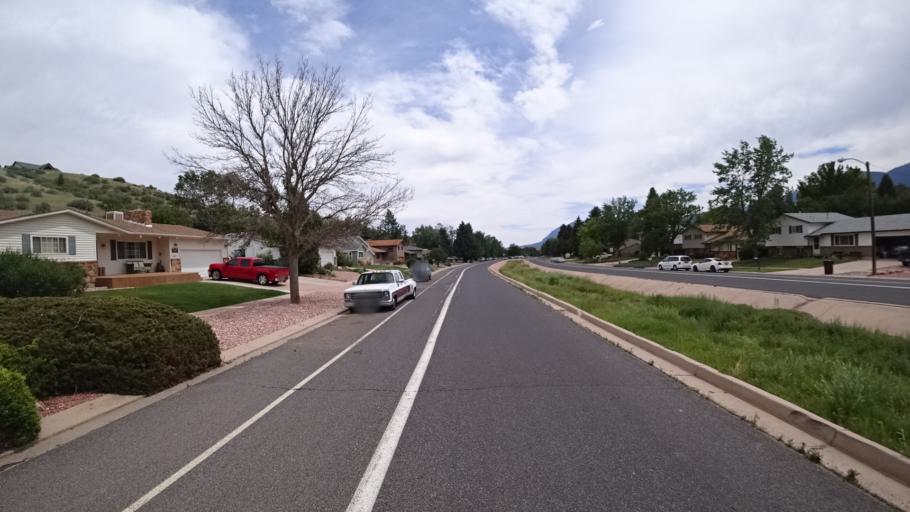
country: US
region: Colorado
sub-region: El Paso County
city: Manitou Springs
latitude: 38.8709
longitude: -104.8691
